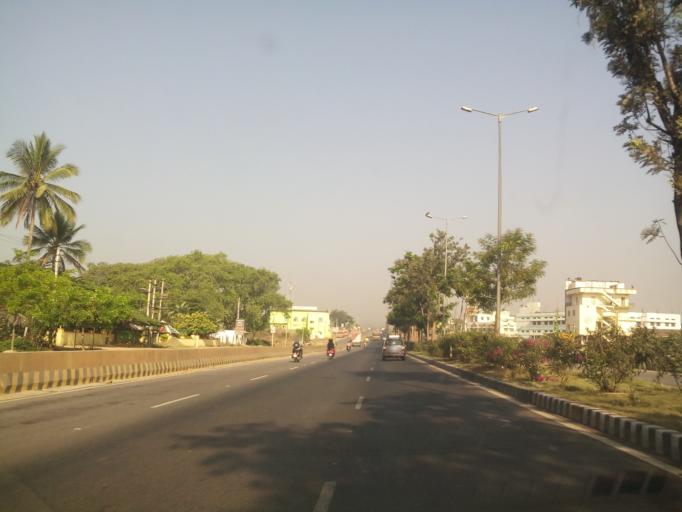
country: IN
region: Karnataka
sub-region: Bangalore Rural
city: Nelamangala
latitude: 13.0886
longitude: 77.4046
